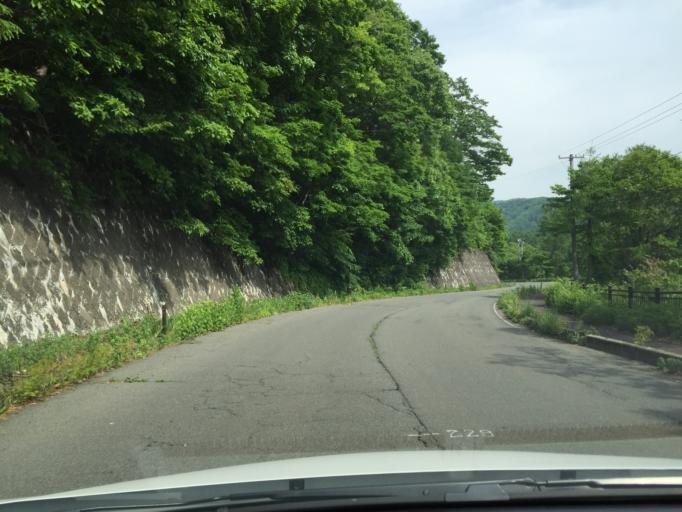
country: JP
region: Fukushima
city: Inawashiro
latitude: 37.7296
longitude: 140.0550
